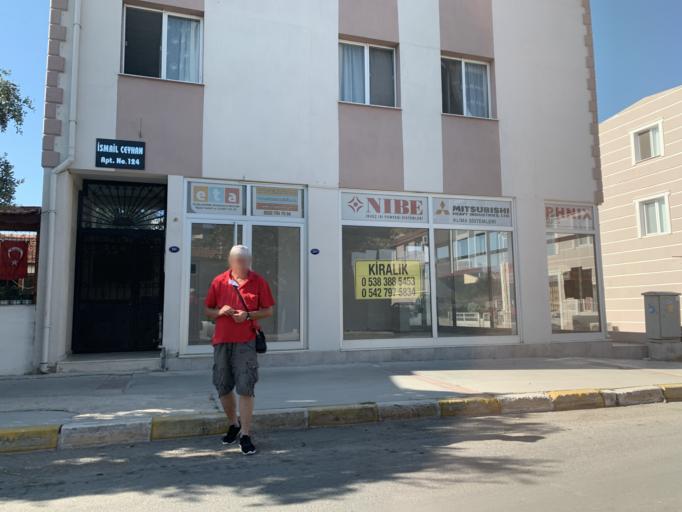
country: TR
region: Izmir
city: Urla
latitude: 38.3209
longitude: 26.7580
